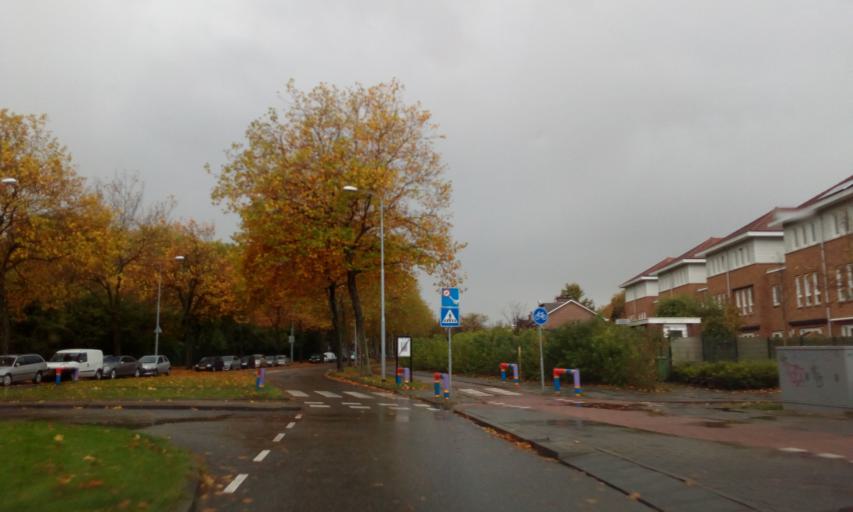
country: NL
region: South Holland
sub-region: Gemeente Rijswijk
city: Rijswijk
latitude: 52.0487
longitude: 4.3371
